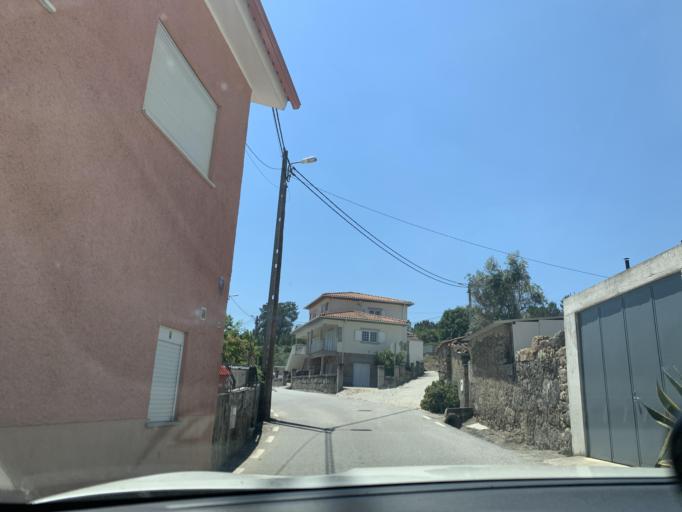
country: PT
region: Viseu
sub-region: Mangualde
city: Mangualde
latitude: 40.5626
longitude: -7.7180
